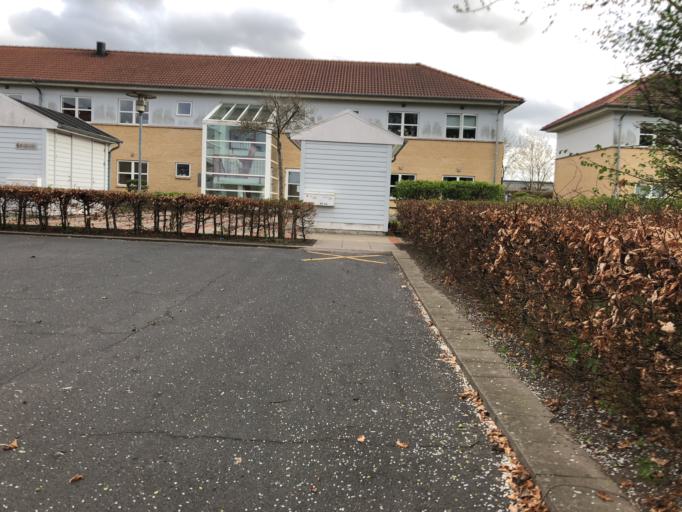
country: DK
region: Zealand
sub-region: Ringsted Kommune
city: Ringsted
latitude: 55.4443
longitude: 11.8083
